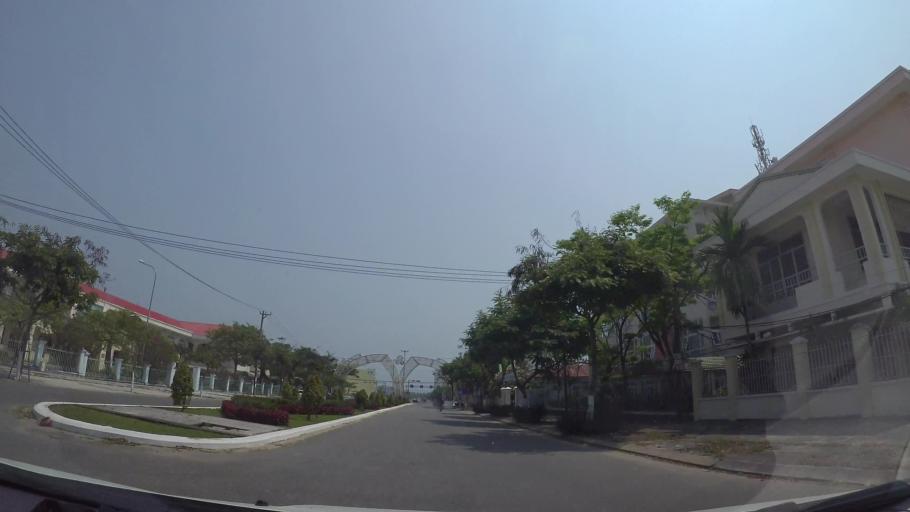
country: VN
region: Da Nang
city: Ngu Hanh Son
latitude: 16.0154
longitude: 108.2534
